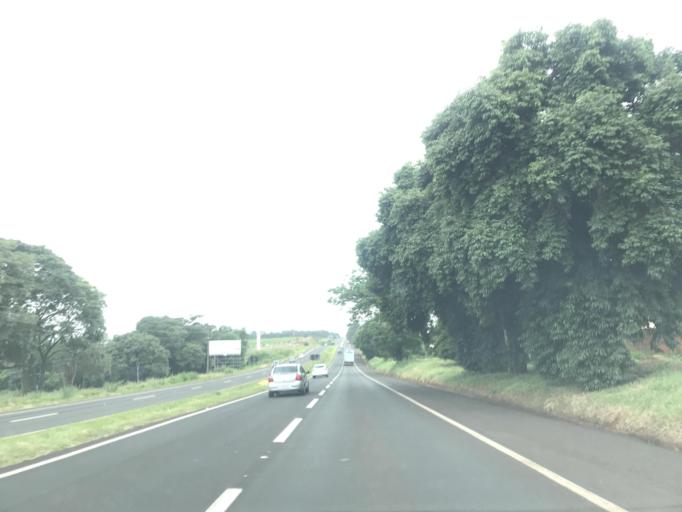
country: BR
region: Parana
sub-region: Paicandu
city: Paicandu
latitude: -23.3845
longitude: -52.0285
